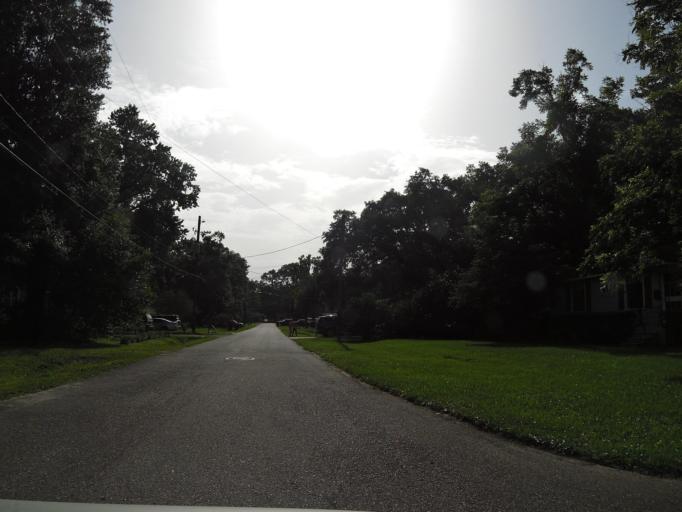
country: US
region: Florida
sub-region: Duval County
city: Jacksonville
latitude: 30.3039
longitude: -81.7244
